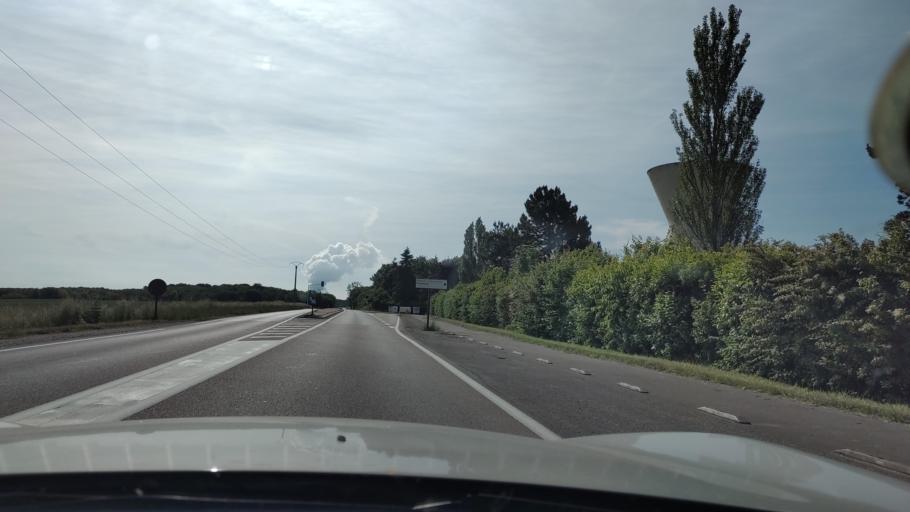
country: FR
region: Ile-de-France
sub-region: Departement de Seine-et-Marne
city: Sourdun
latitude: 48.5340
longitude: 3.3701
